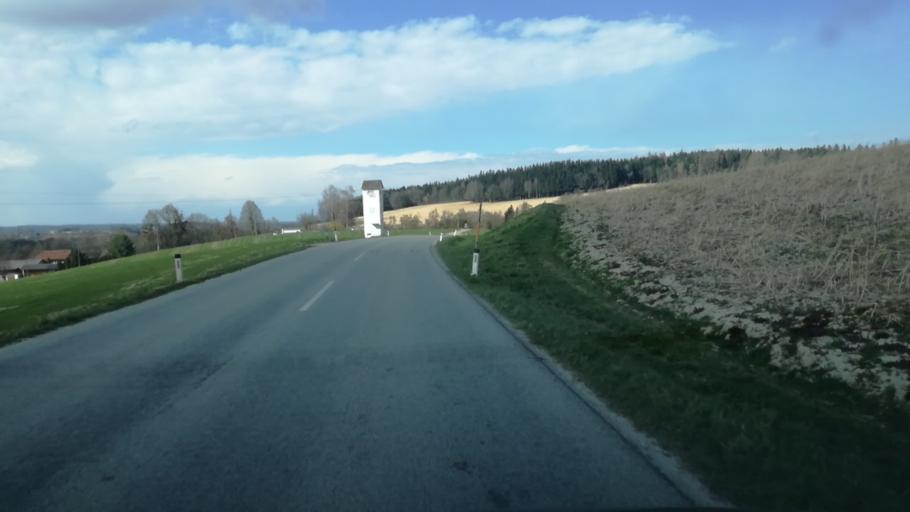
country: AT
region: Upper Austria
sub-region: Politischer Bezirk Ried im Innkreis
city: Ried im Innkreis
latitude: 48.1715
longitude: 13.4839
